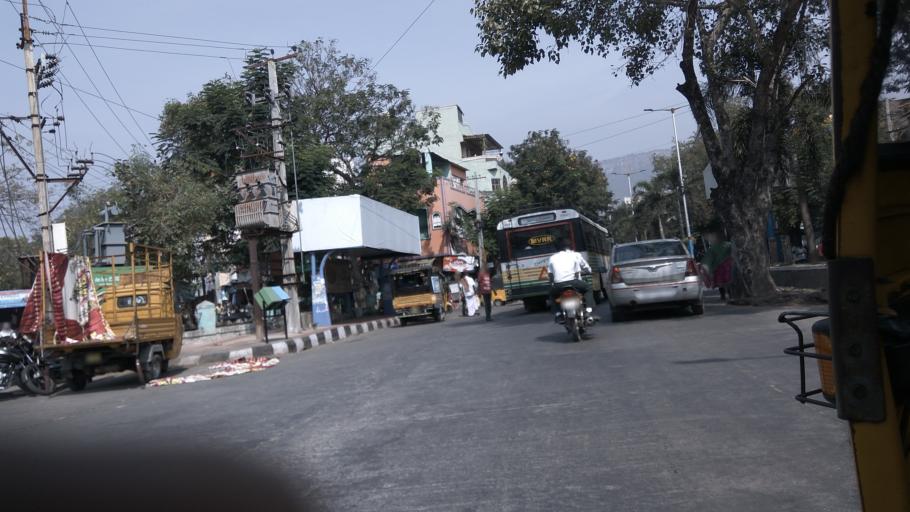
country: IN
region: Andhra Pradesh
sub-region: Chittoor
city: Tirupati
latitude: 13.6354
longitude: 79.4127
